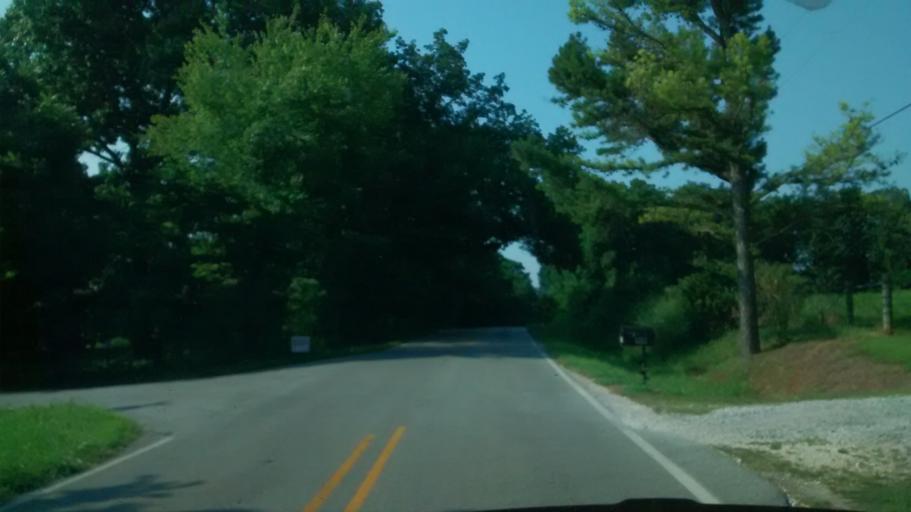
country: US
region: Arkansas
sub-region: Washington County
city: Farmington
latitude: 36.0613
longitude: -94.2537
